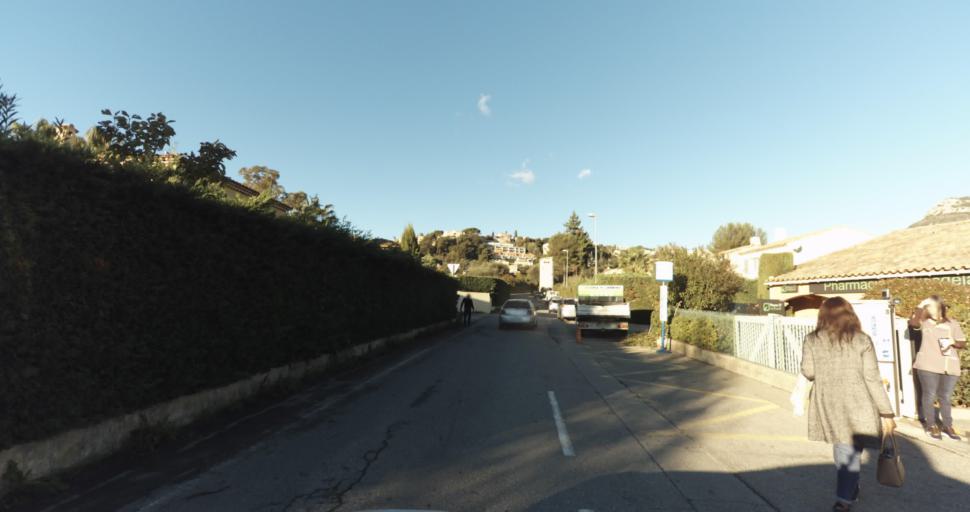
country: FR
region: Provence-Alpes-Cote d'Azur
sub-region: Departement des Alpes-Maritimes
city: Vence
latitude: 43.7177
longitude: 7.1291
